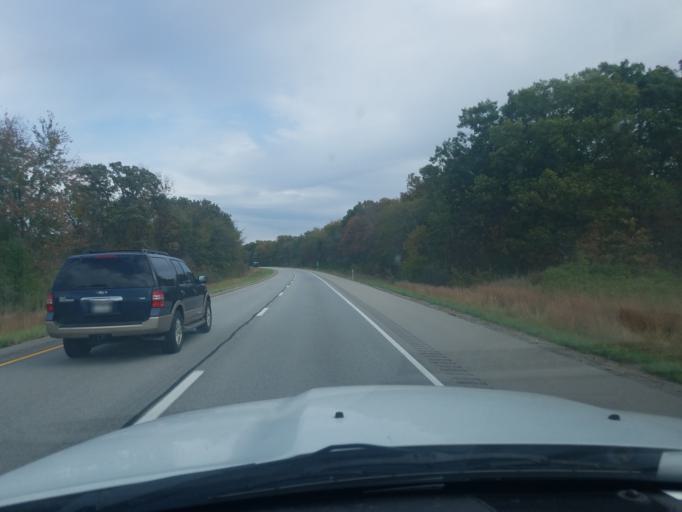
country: US
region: Indiana
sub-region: Warrick County
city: Chandler
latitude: 38.1697
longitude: -87.4340
